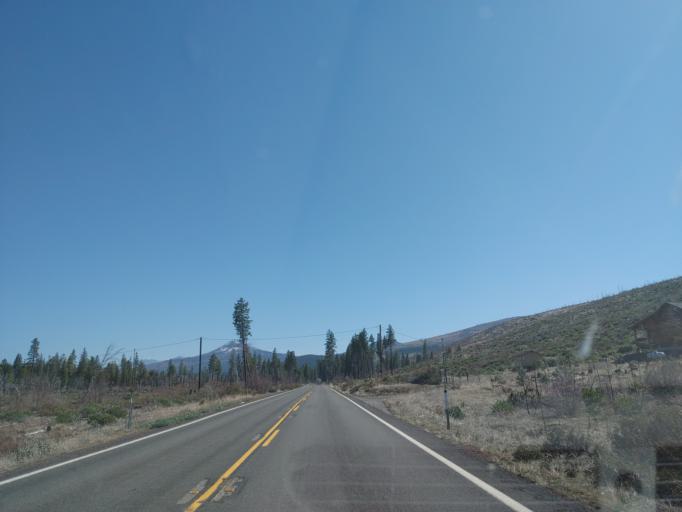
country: US
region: California
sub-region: Shasta County
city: Burney
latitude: 40.7881
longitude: -121.5060
